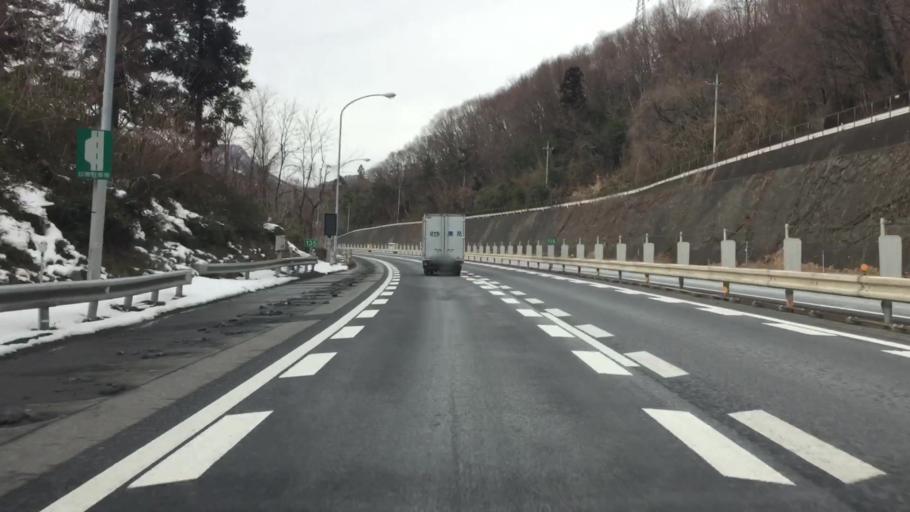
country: JP
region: Gunma
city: Numata
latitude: 36.6975
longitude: 138.9912
